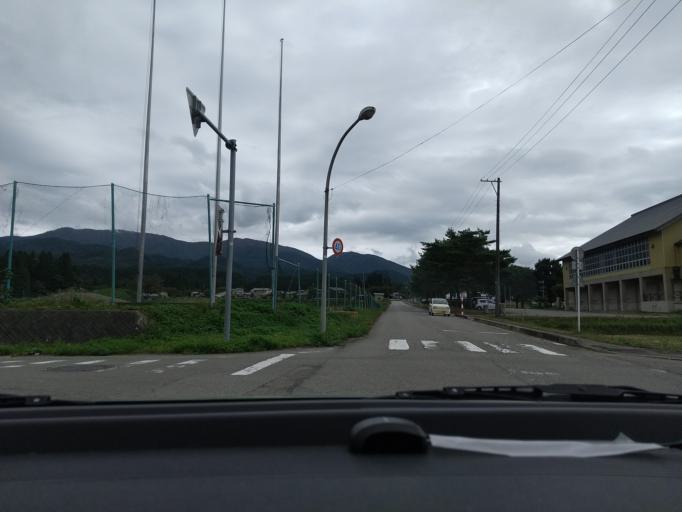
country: JP
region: Akita
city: Kakunodatemachi
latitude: 39.5877
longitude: 140.6074
